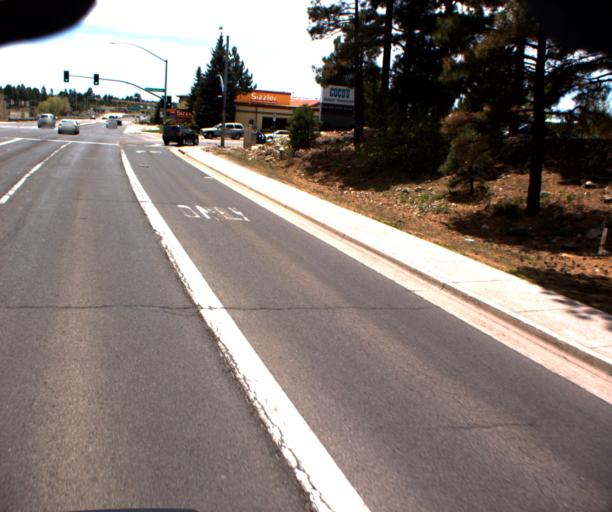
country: US
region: Arizona
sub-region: Coconino County
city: Flagstaff
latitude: 35.1796
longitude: -111.6614
